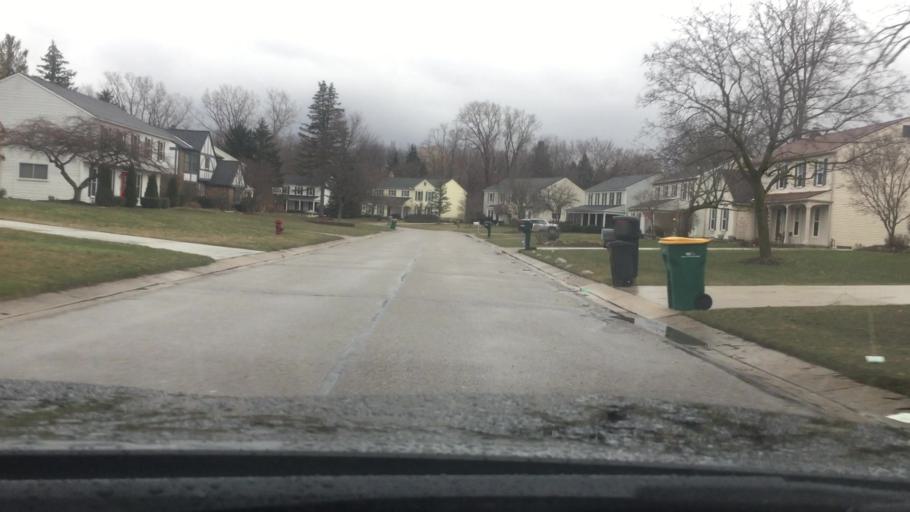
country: US
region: Michigan
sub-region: Oakland County
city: Farmington Hills
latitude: 42.5005
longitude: -83.4070
